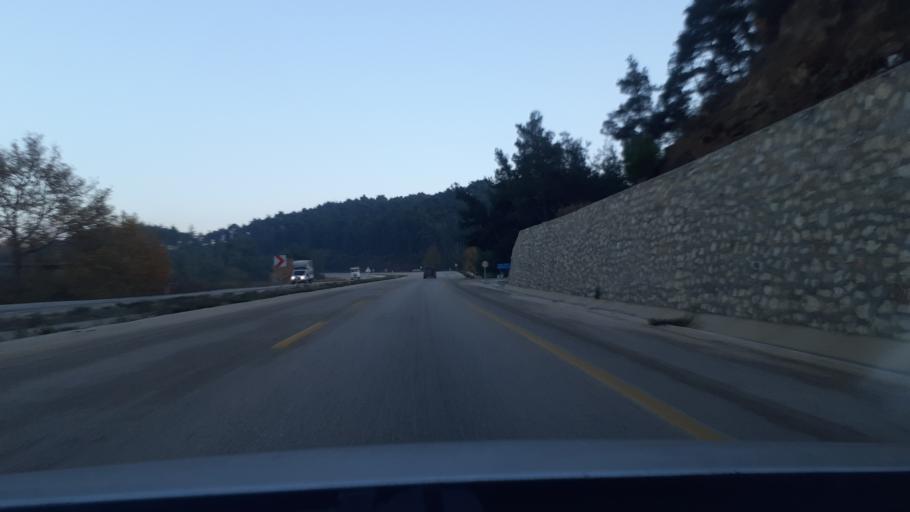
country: TR
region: Hatay
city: Yayladagi
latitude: 35.8926
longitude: 36.0852
